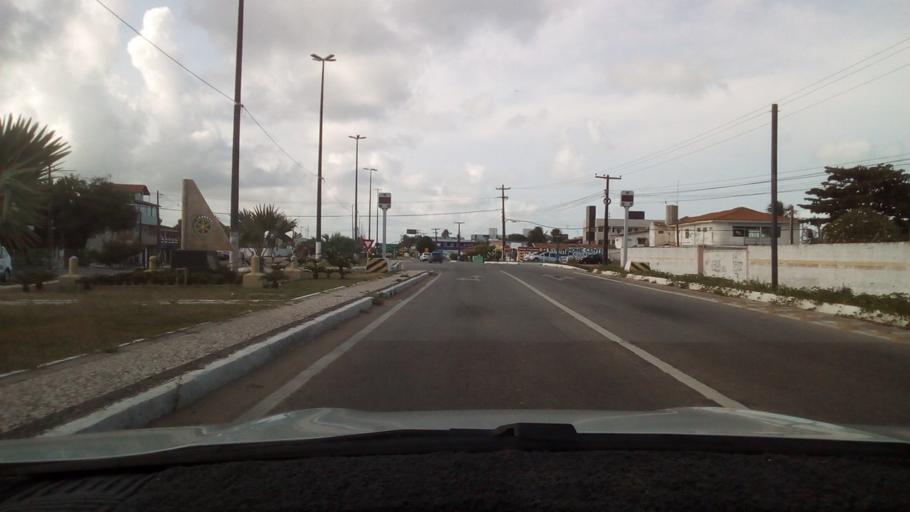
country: BR
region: Paraiba
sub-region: Cabedelo
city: Cabedelo
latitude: -6.9853
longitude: -34.8289
